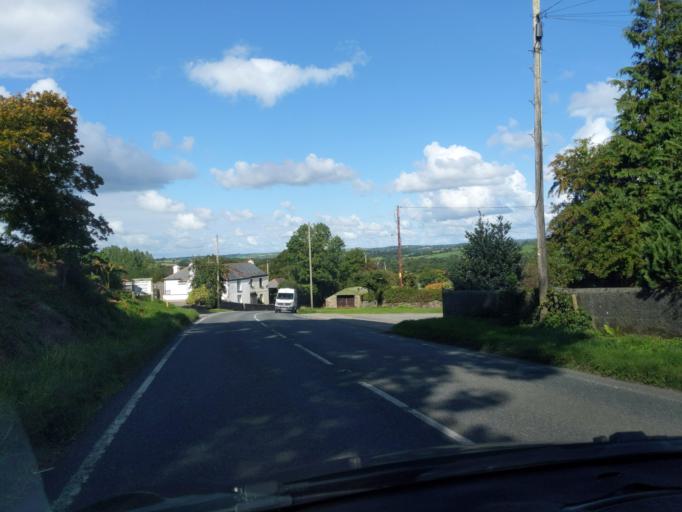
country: GB
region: England
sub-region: Cornwall
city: Launceston
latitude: 50.6493
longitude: -4.3492
